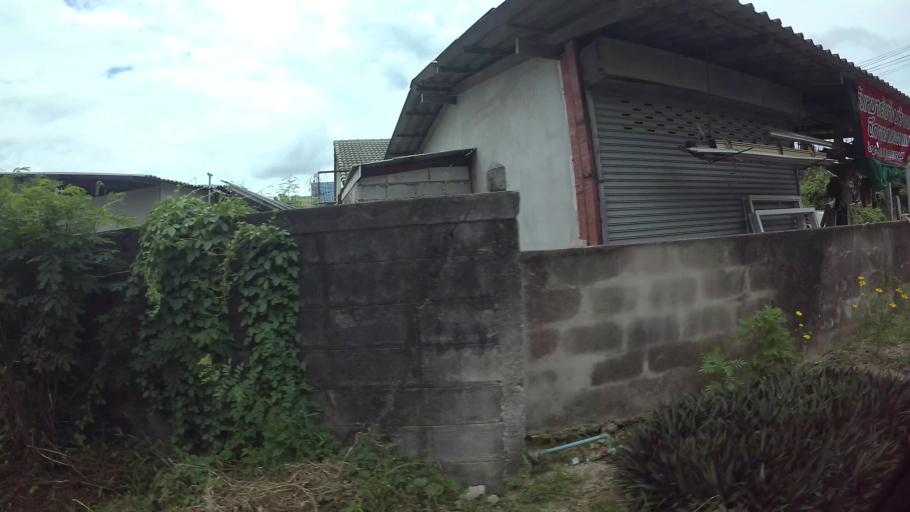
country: TH
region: Chon Buri
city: Sattahip
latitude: 12.7575
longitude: 100.8907
